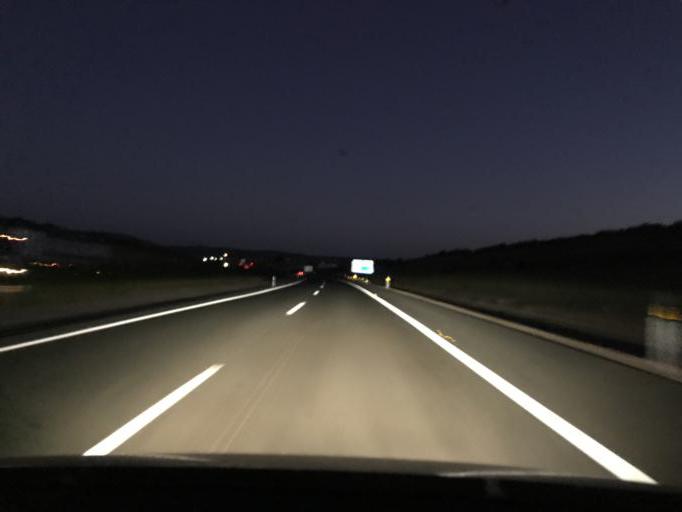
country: ES
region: Andalusia
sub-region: Provincia de Malaga
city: Antequera
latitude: 37.1011
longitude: -4.5544
